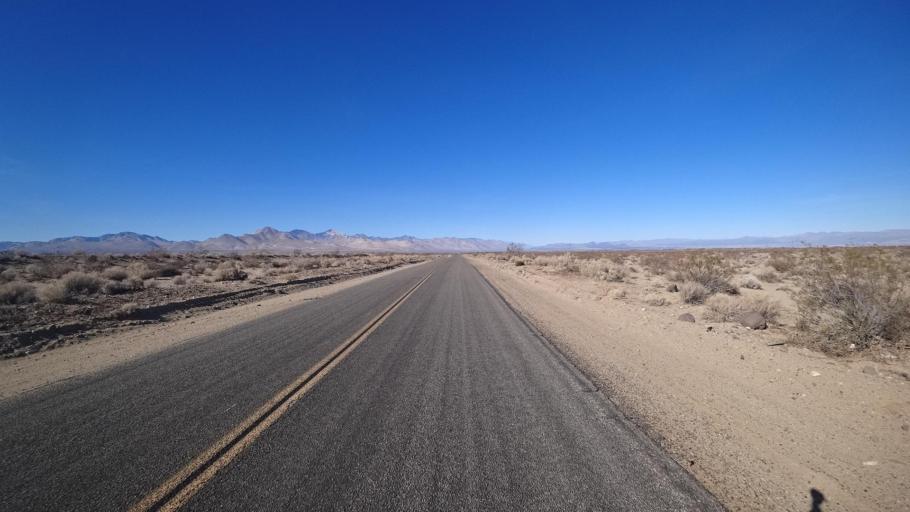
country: US
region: California
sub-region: Kern County
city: China Lake Acres
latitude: 35.5725
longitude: -117.7823
